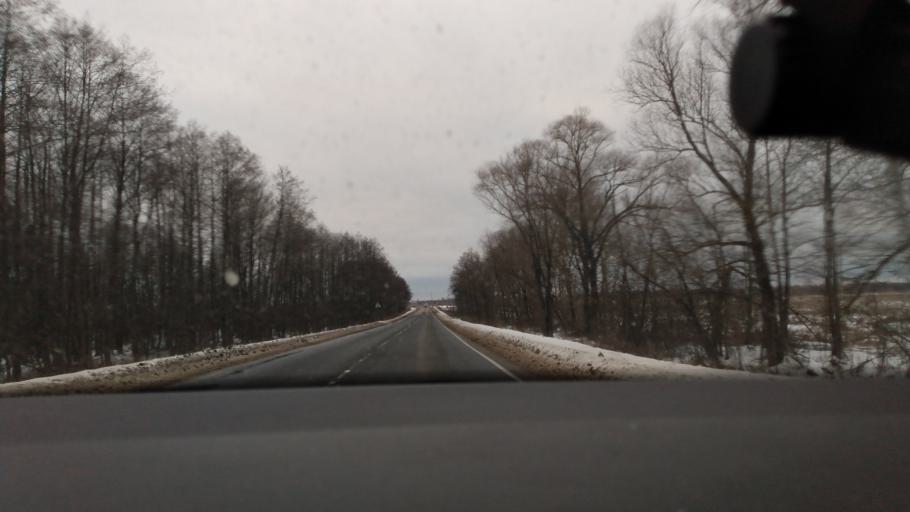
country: RU
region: Moskovskaya
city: Krasnaya Poyma
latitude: 55.1369
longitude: 39.2002
